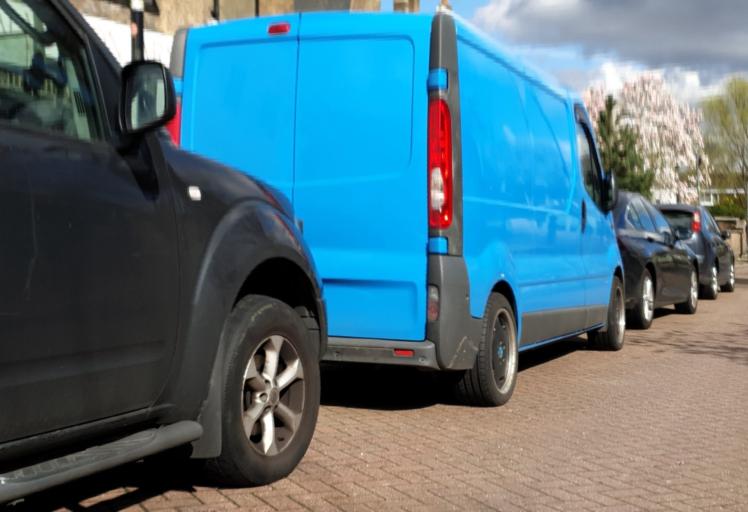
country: GB
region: England
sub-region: Greater London
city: Camberwell
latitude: 51.4654
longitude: -0.0590
